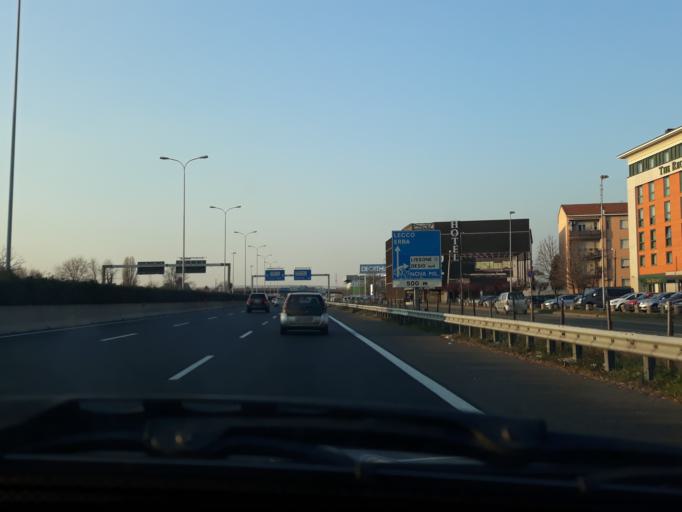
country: IT
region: Lombardy
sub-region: Provincia di Monza e Brianza
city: Lissone
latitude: 45.6031
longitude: 9.2303
